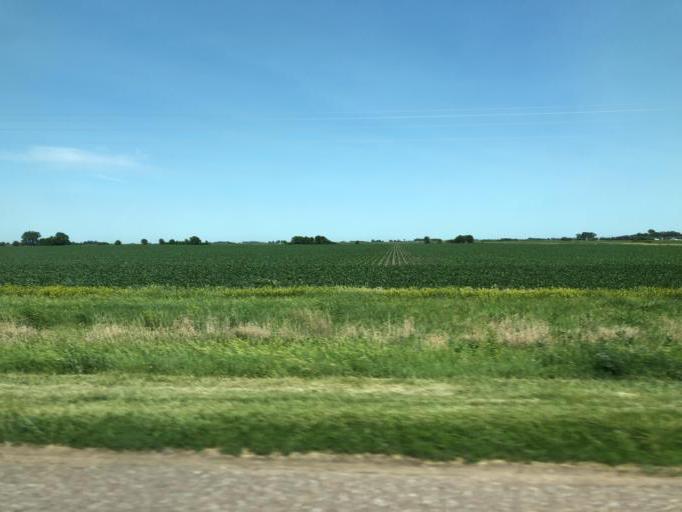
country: US
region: Nebraska
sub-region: Fillmore County
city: Geneva
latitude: 40.6116
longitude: -97.5957
